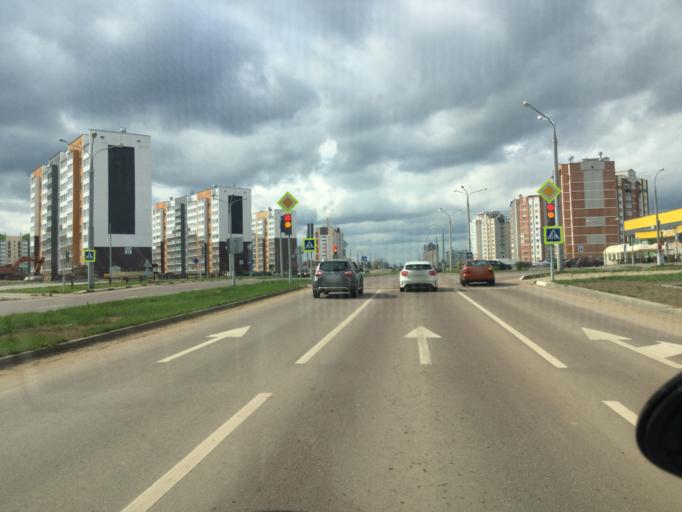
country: BY
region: Vitebsk
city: Vitebsk
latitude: 55.1638
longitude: 30.2771
